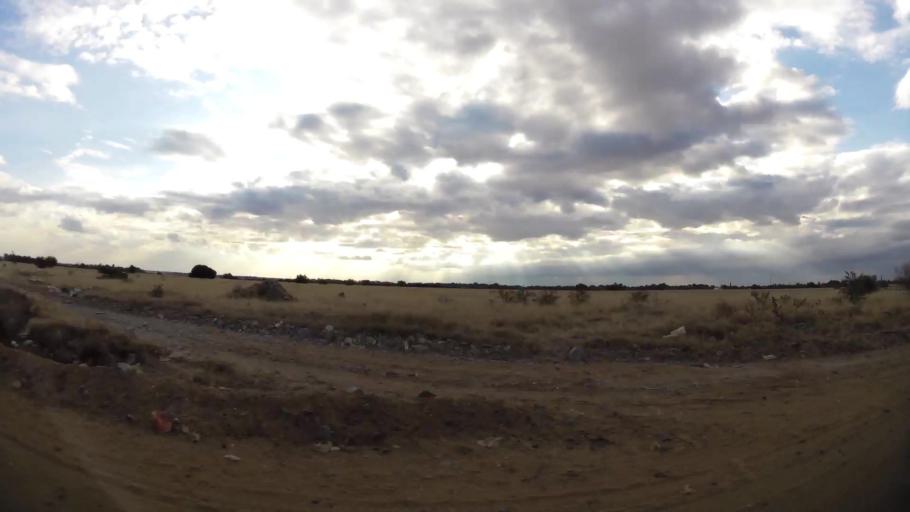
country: ZA
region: Orange Free State
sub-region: Lejweleputswa District Municipality
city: Welkom
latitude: -28.0096
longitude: 26.7279
